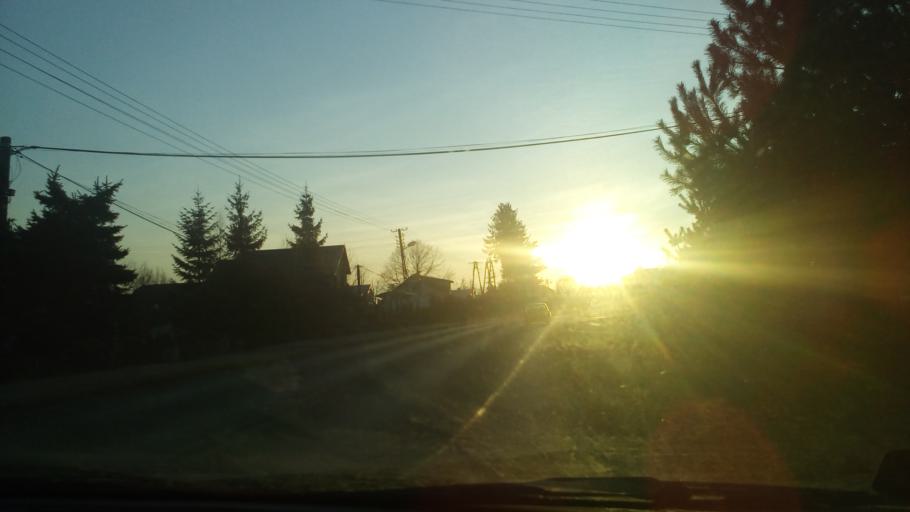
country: PL
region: Lesser Poland Voivodeship
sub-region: Powiat nowosadecki
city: Chelmiec
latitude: 49.6111
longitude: 20.6599
